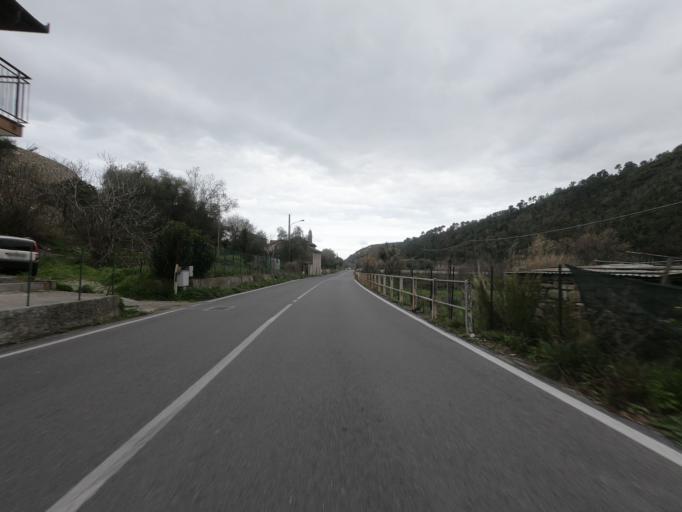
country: IT
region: Liguria
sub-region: Provincia di Savona
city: Villafranca
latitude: 43.9983
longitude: 8.1113
